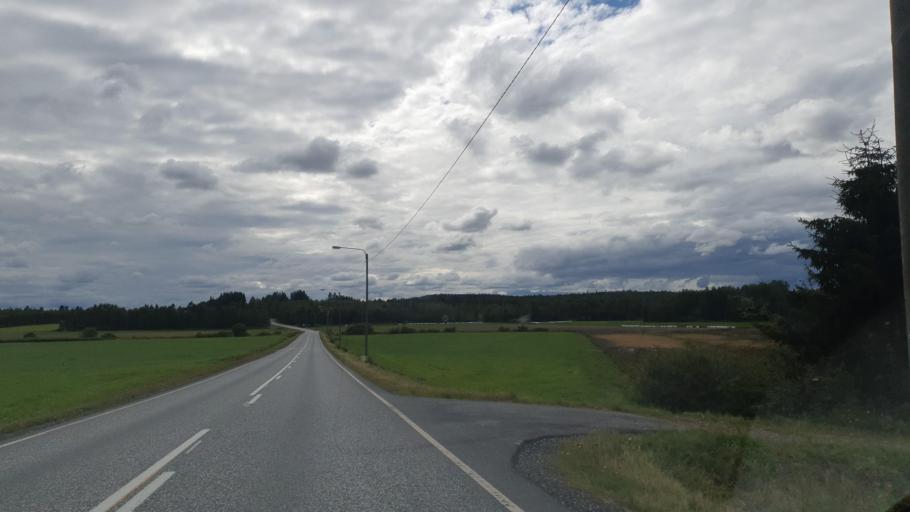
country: FI
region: Northern Savo
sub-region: Ylae-Savo
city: Iisalmi
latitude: 63.5204
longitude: 27.1377
